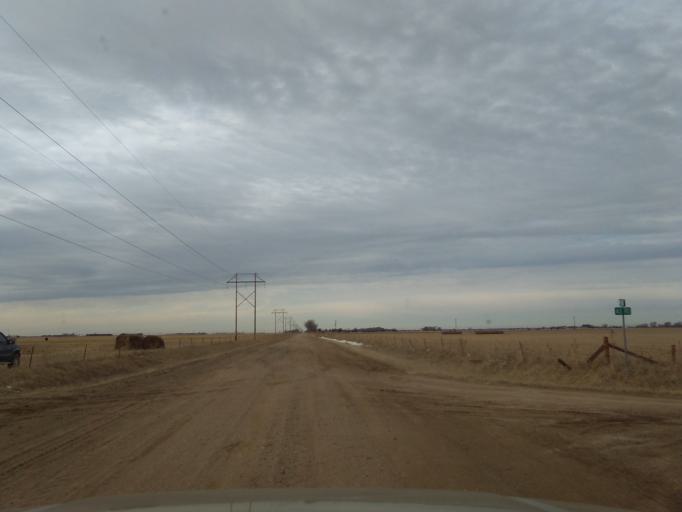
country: US
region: Nebraska
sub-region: Buffalo County
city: Shelton
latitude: 40.6548
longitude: -98.7432
